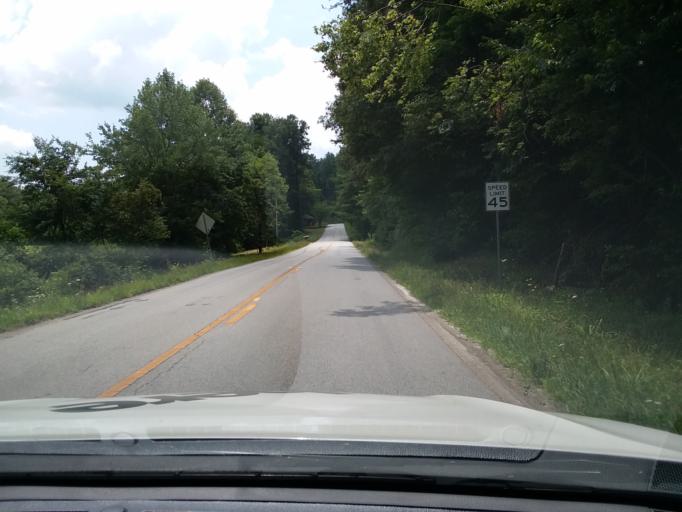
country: US
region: Georgia
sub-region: Rabun County
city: Mountain City
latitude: 34.9964
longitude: -83.1964
